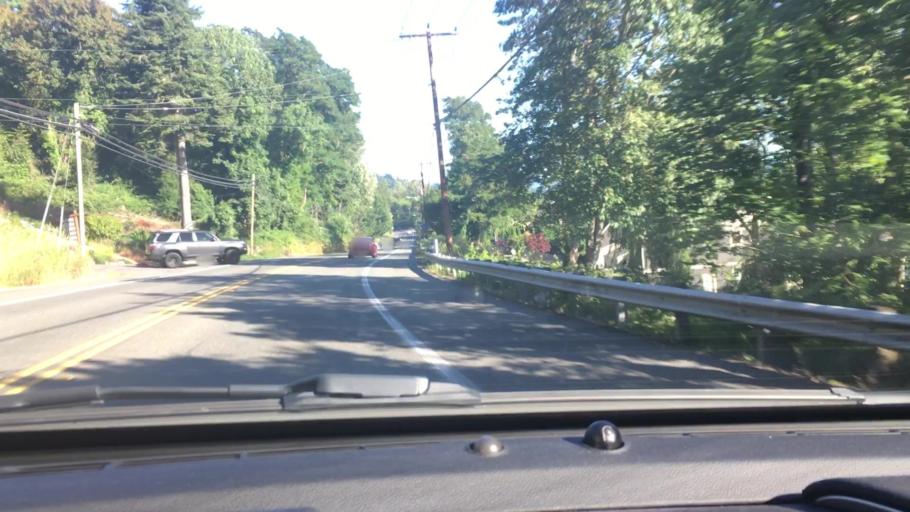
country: US
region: Washington
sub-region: King County
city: Sammamish
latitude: 47.6451
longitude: -122.0838
